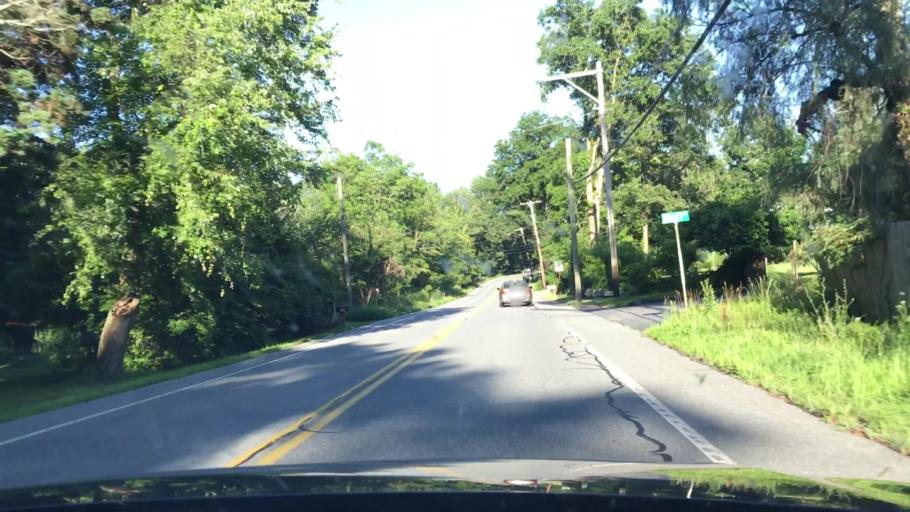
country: US
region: New York
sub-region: Westchester County
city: Heritage Hills
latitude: 41.3683
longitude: -73.6898
